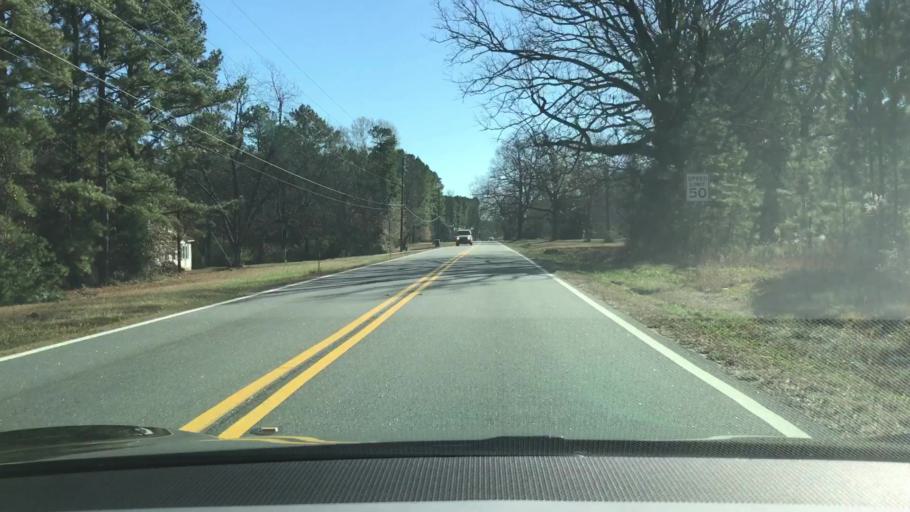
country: US
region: Georgia
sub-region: Walton County
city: Monroe
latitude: 33.8715
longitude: -83.7576
